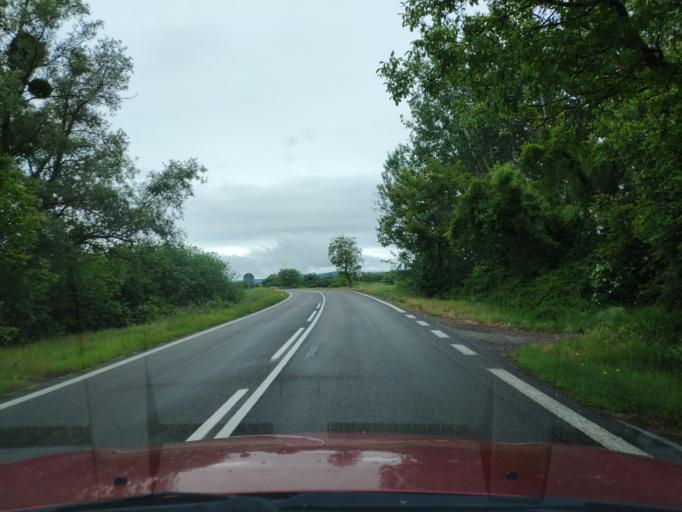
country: HU
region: Borsod-Abauj-Zemplen
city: Ricse
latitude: 48.4335
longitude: 21.8901
